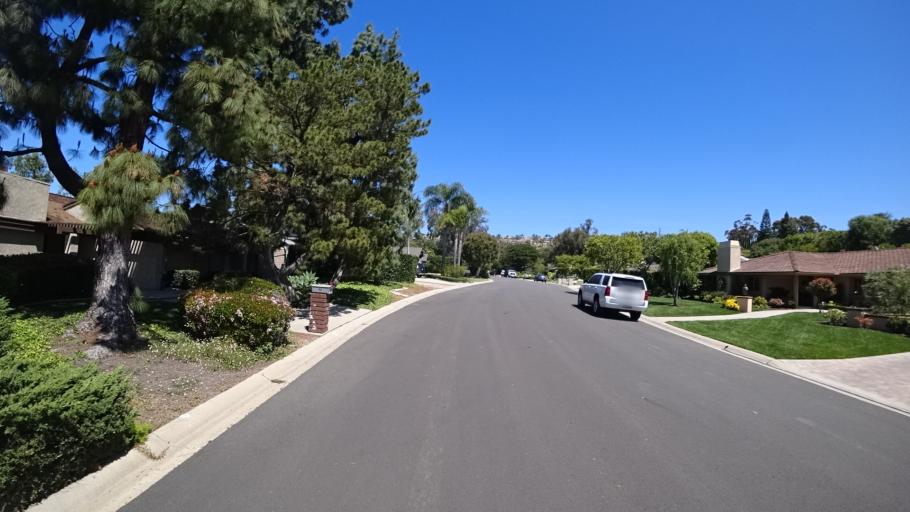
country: US
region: California
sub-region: Orange County
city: Villa Park
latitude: 33.8265
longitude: -117.7976
